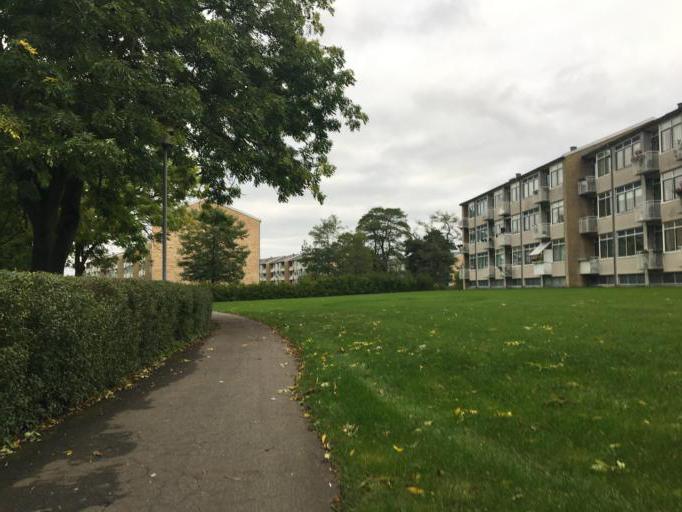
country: DK
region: Capital Region
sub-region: Tarnby Kommune
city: Tarnby
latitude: 55.6325
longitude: 12.6336
